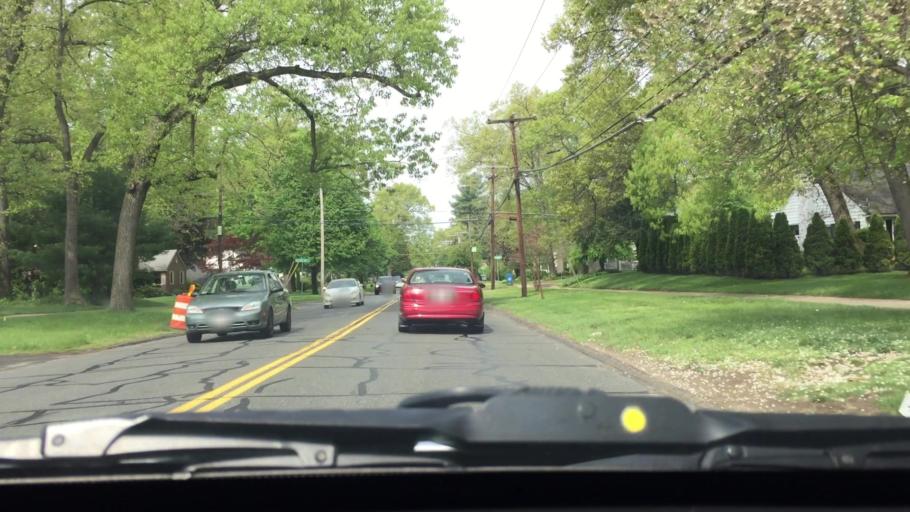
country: US
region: Massachusetts
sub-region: Hampden County
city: Longmeadow
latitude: 42.0575
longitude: -72.5643
